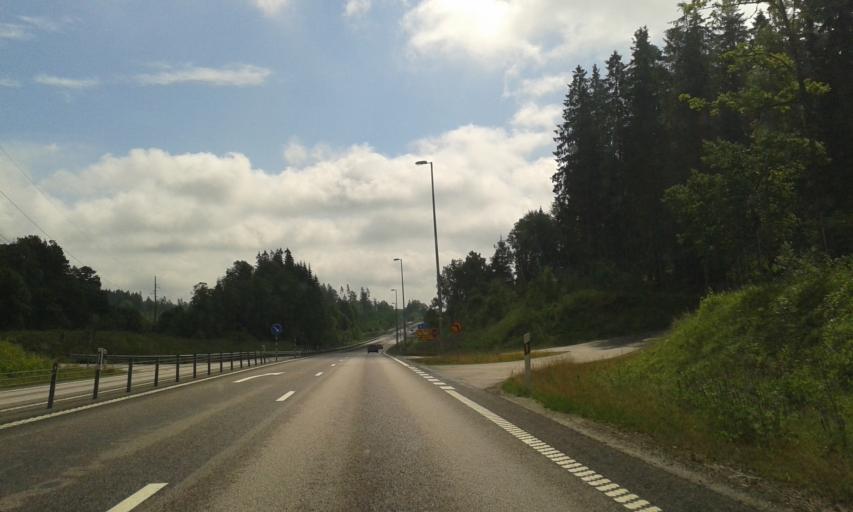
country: SE
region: Vaestra Goetaland
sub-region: Boras Kommun
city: Ganghester
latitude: 57.6756
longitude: 12.9847
